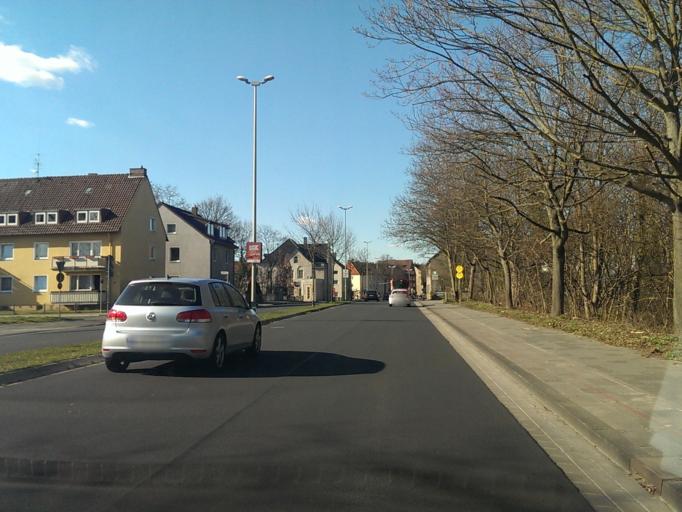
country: DE
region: Lower Saxony
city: Hildesheim
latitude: 52.1473
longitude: 9.9390
